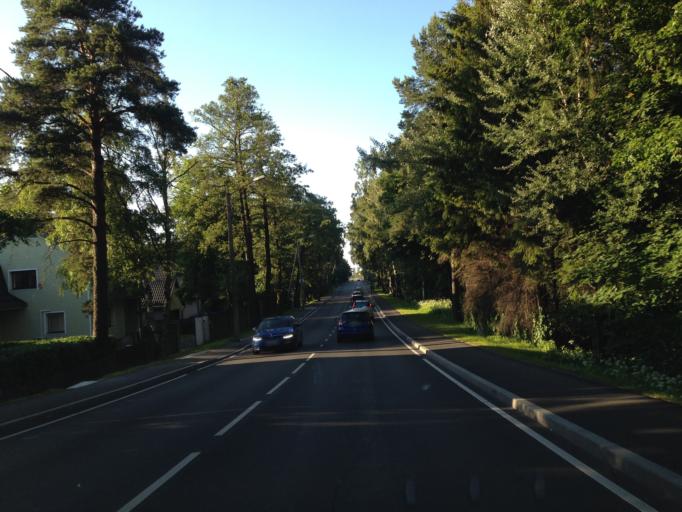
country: EE
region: Harju
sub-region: Saue vald
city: Laagri
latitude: 59.3878
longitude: 24.6410
